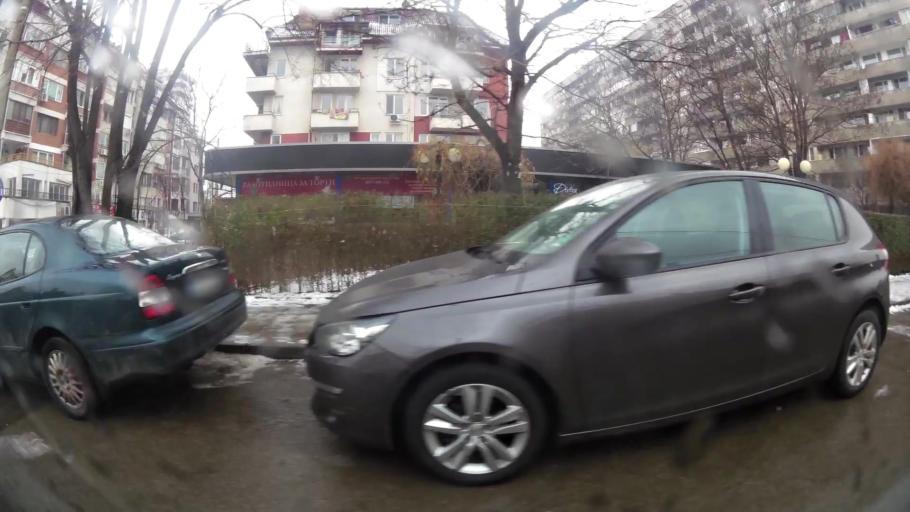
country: BG
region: Sofia-Capital
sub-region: Stolichna Obshtina
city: Sofia
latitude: 42.6768
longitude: 23.2855
